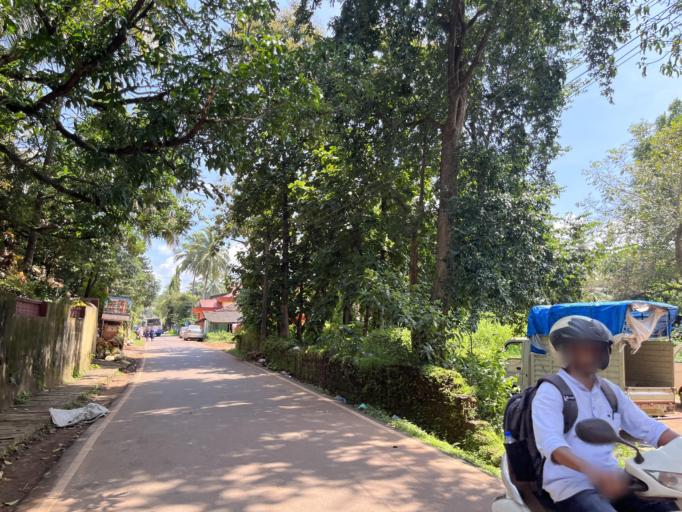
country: IN
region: Goa
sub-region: North Goa
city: Ponda
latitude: 15.4000
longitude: 74.0128
